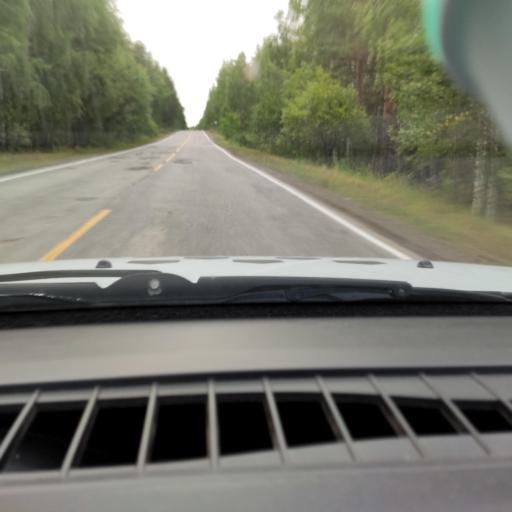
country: RU
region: Chelyabinsk
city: Ozersk
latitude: 55.8240
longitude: 60.6450
